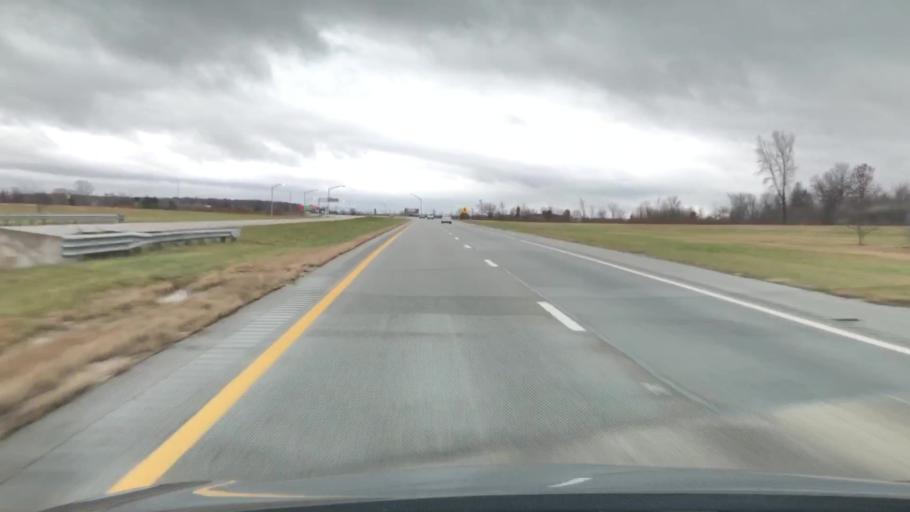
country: US
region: Ohio
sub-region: Wood County
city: Walbridge
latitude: 41.5878
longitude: -83.4770
